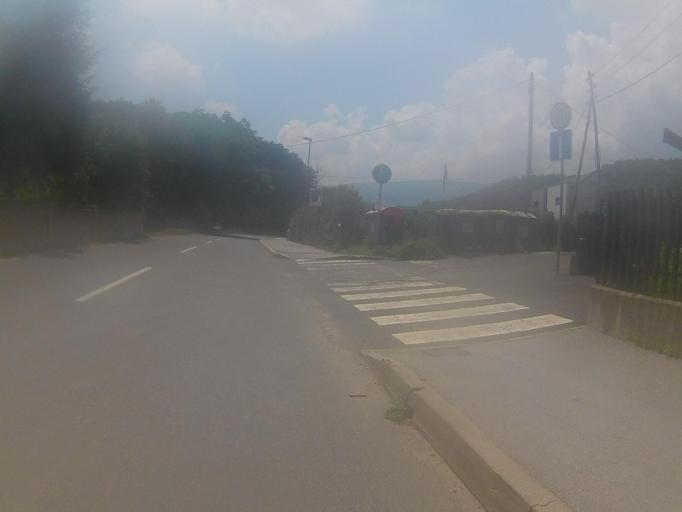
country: SI
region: Maribor
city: Kamnica
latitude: 46.5818
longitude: 15.6148
